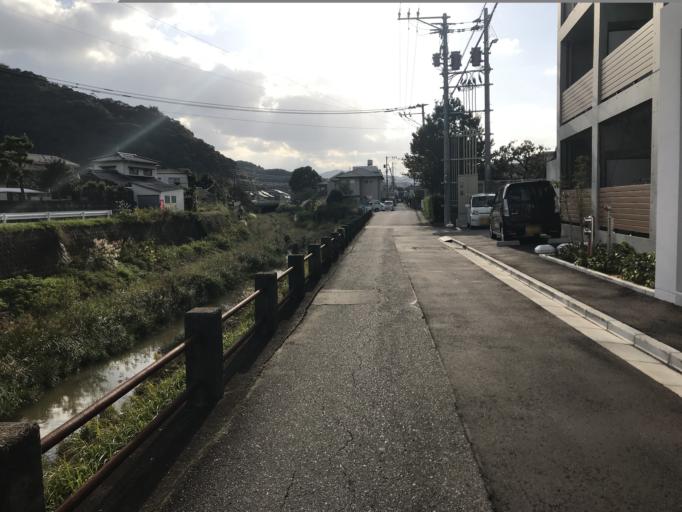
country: JP
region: Saga Prefecture
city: Takeocho-takeo
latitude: 33.1927
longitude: 130.0178
